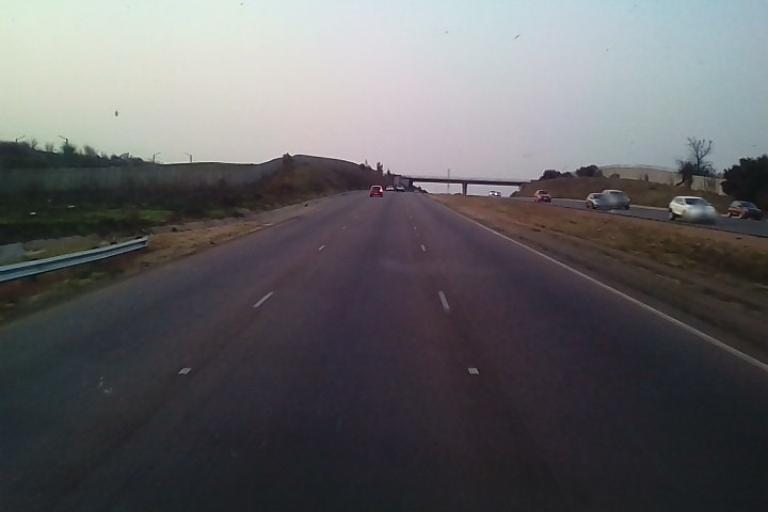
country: ZA
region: Gauteng
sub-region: City of Tshwane Metropolitan Municipality
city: Centurion
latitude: -25.8046
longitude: 28.1806
